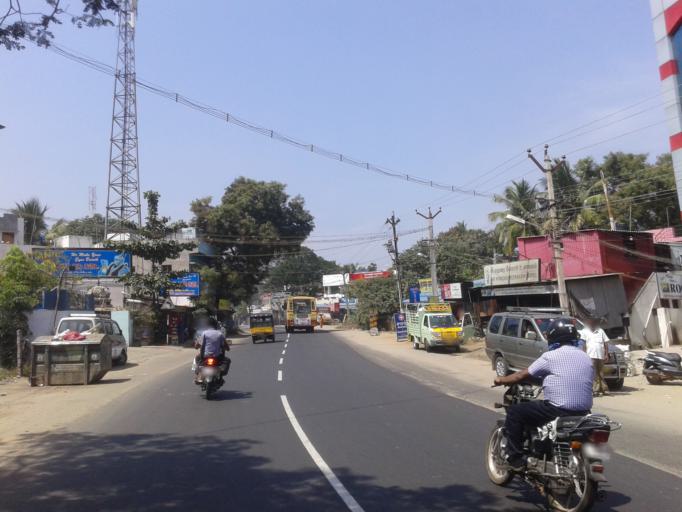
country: IN
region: Tamil Nadu
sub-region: Madurai
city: Madurai
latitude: 9.9340
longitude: 78.0822
